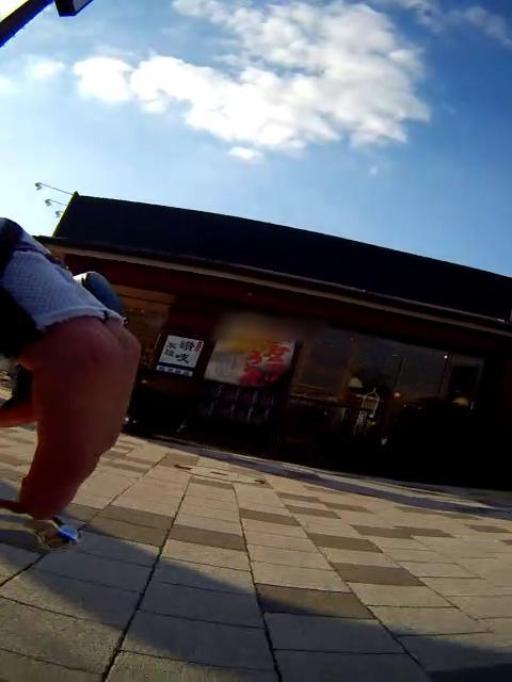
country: JP
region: Hyogo
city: Itami
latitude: 34.7686
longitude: 135.3801
